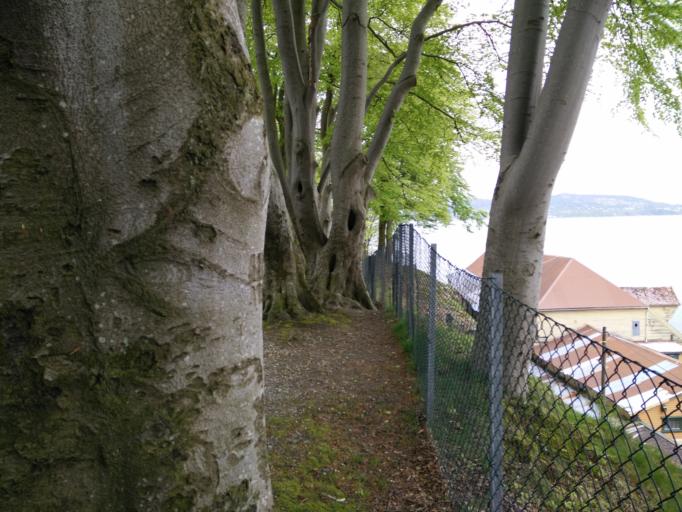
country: NO
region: Hordaland
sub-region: Bergen
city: Bergen
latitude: 60.4004
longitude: 5.3050
